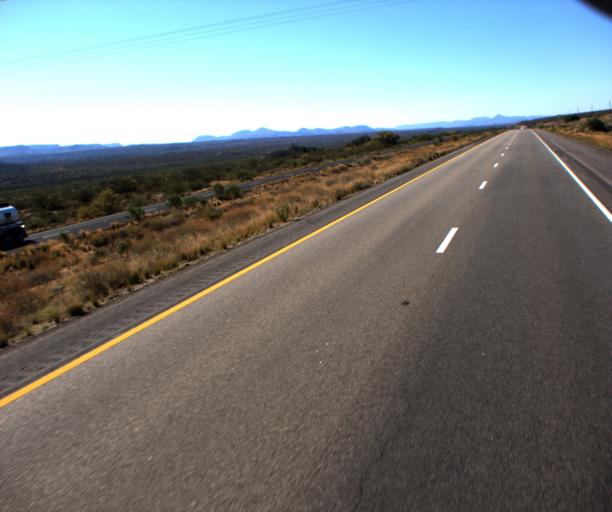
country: US
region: Arizona
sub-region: Mohave County
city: Kingman
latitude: 34.8529
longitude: -113.6388
